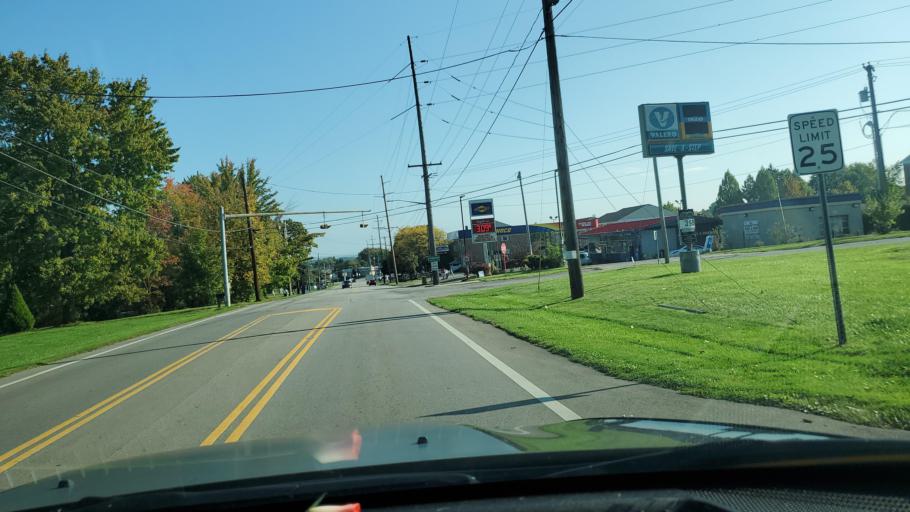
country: US
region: Ohio
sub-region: Trumbull County
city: Hubbard
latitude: 41.1542
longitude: -80.5880
